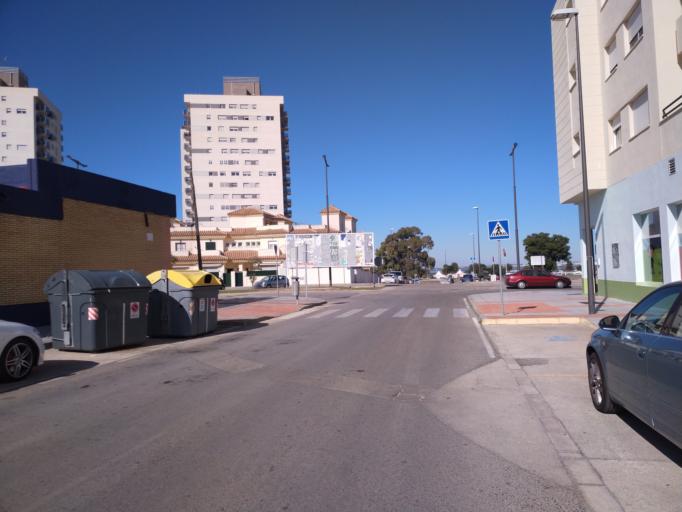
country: ES
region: Andalusia
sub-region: Provincia de Cadiz
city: San Fernando
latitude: 36.4823
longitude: -6.1983
